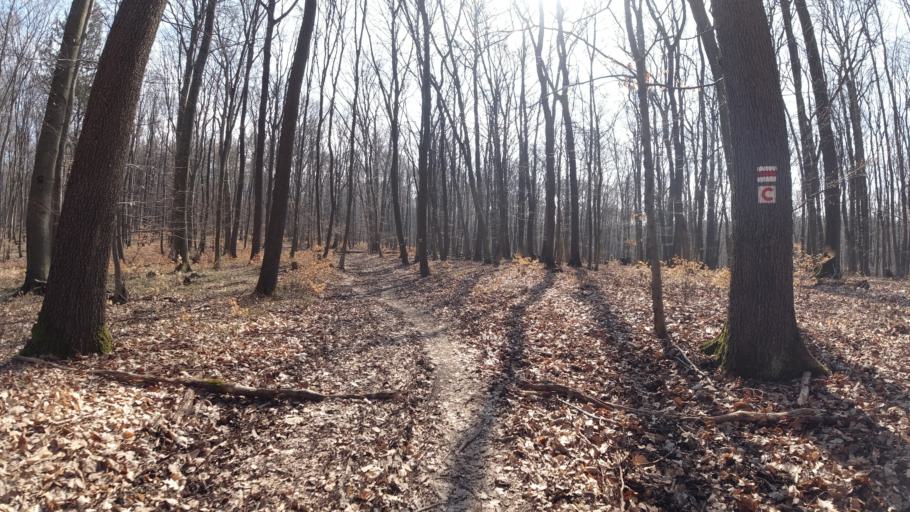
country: SK
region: Trnavsky
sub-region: Okres Trnava
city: Piestany
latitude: 48.5877
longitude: 17.9156
